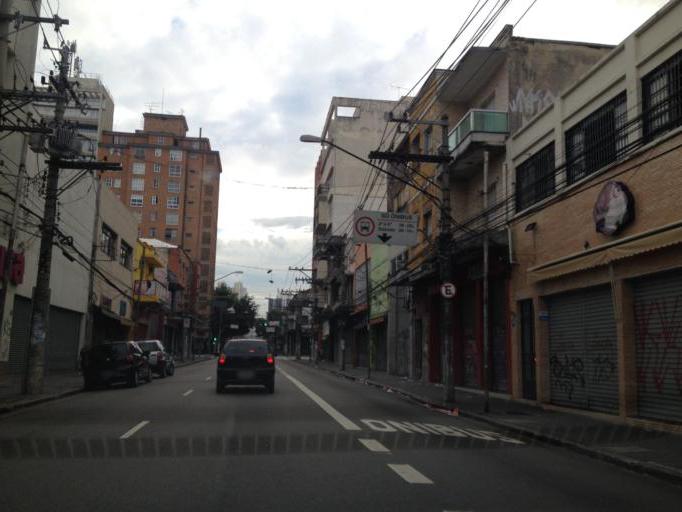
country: BR
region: Sao Paulo
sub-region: Sao Paulo
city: Sao Paulo
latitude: -23.5658
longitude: -46.6913
